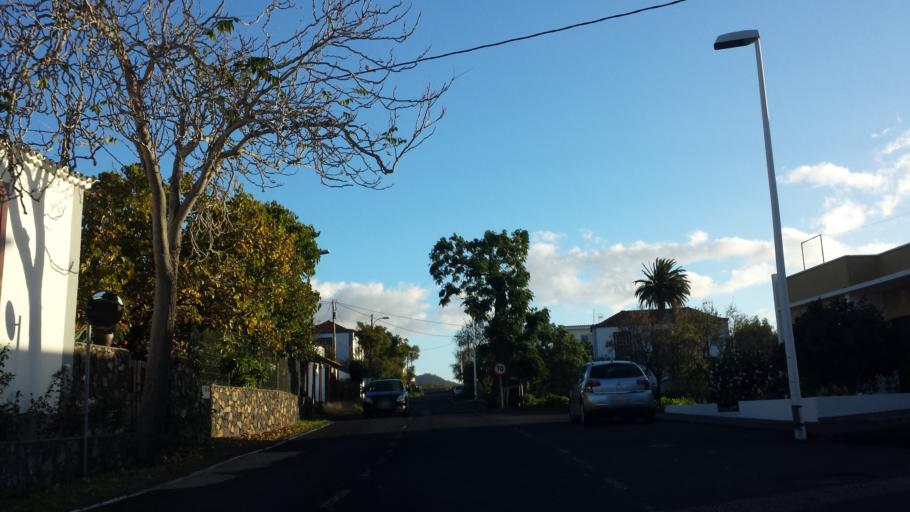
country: ES
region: Canary Islands
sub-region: Provincia de Santa Cruz de Tenerife
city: El Paso
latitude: 28.6325
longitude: -17.8880
